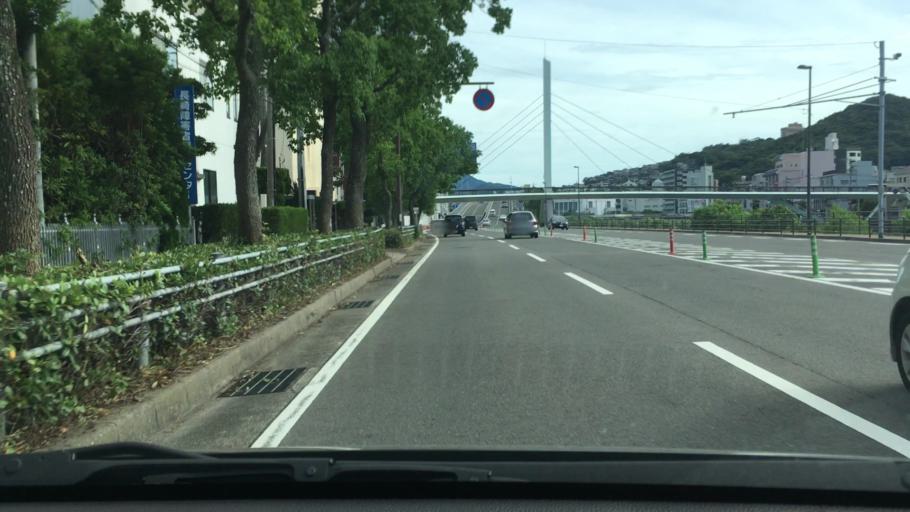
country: JP
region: Nagasaki
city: Nagasaki-shi
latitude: 32.7673
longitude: 129.8623
